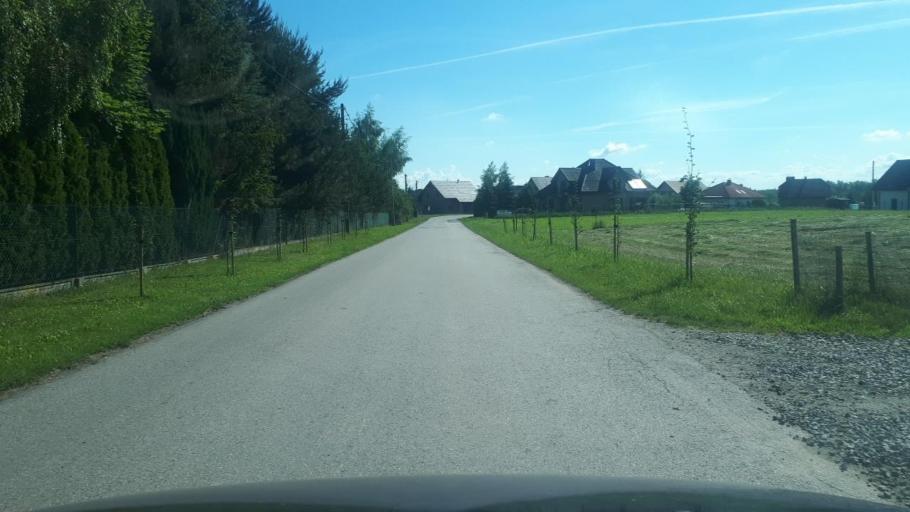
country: PL
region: Silesian Voivodeship
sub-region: Powiat bielski
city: Pisarzowice
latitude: 49.8754
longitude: 19.1278
